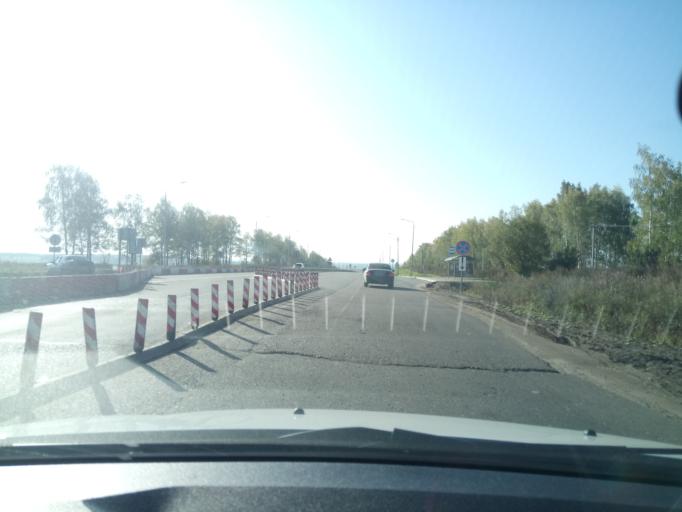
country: RU
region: Nizjnij Novgorod
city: Dal'neye Konstantinovo
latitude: 55.9983
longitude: 43.9680
